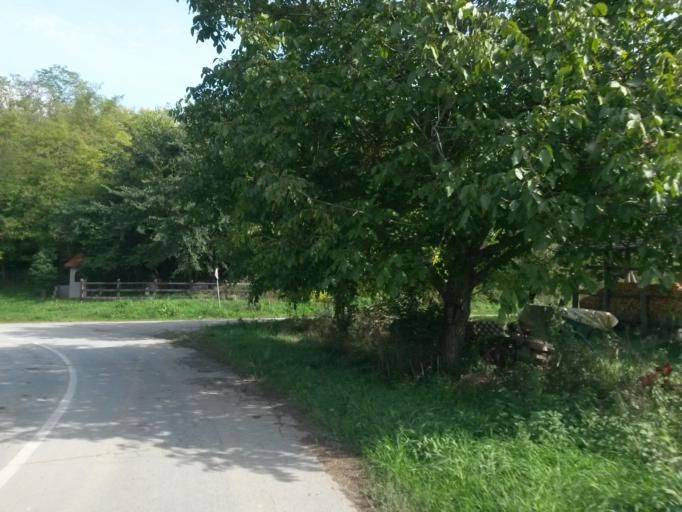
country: HR
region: Vukovarsko-Srijemska
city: Ilok
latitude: 45.2122
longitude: 19.3863
